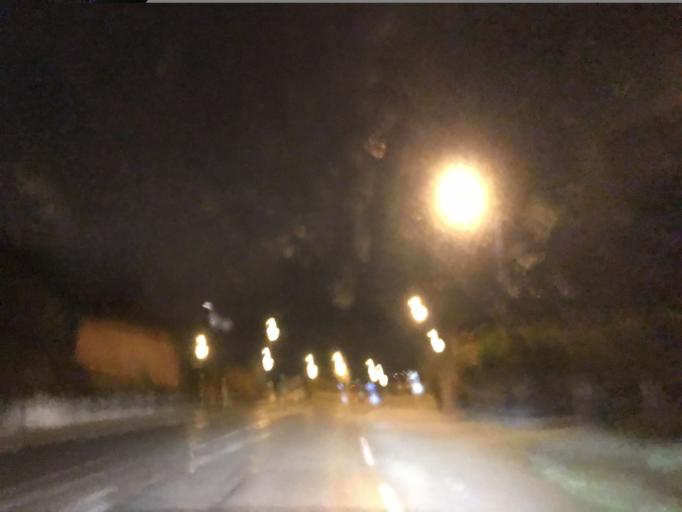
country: FR
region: Auvergne
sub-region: Departement de l'Allier
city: Hauterive
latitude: 46.0784
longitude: 3.4412
